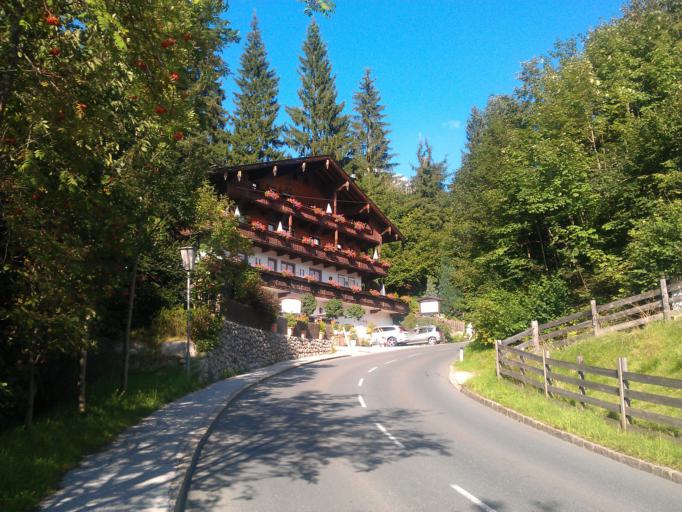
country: AT
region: Tyrol
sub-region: Politischer Bezirk Kufstein
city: Alpbach
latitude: 47.3969
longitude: 11.9388
